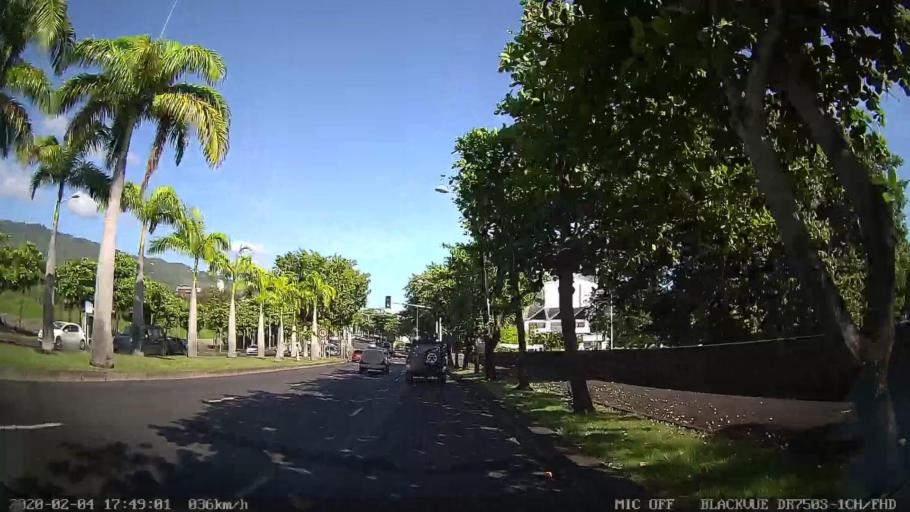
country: RE
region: Reunion
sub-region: Reunion
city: Saint-Denis
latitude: -20.8909
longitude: 55.4662
